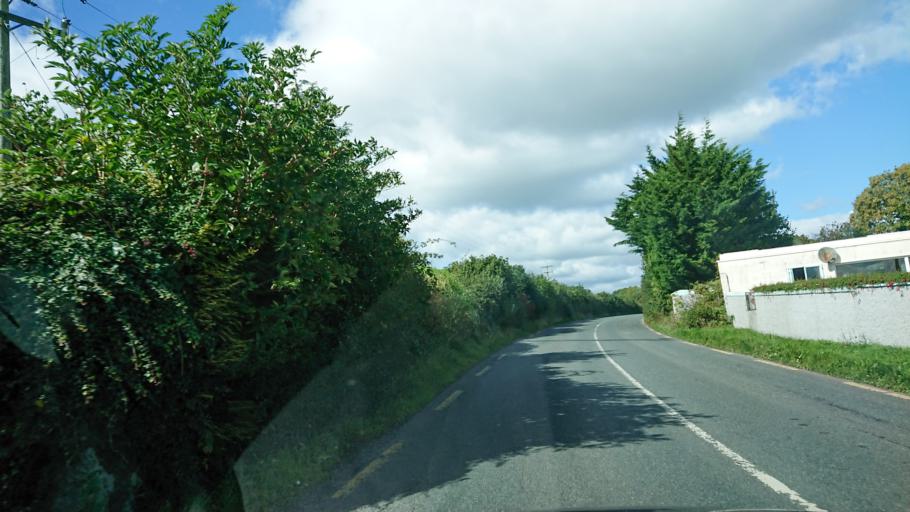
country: IE
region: Munster
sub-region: Waterford
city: Dungarvan
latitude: 52.1111
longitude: -7.6783
